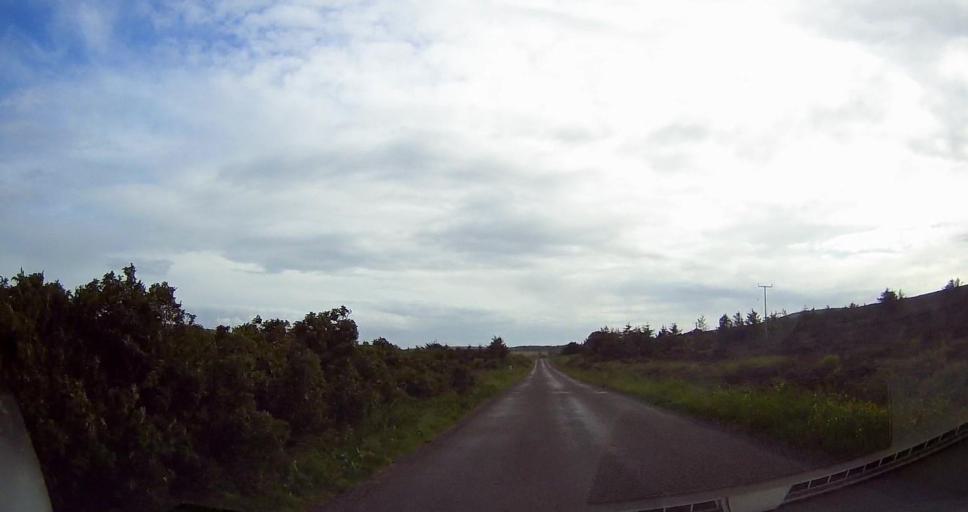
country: GB
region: Scotland
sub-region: Orkney Islands
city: Stromness
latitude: 58.7964
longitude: -3.2527
